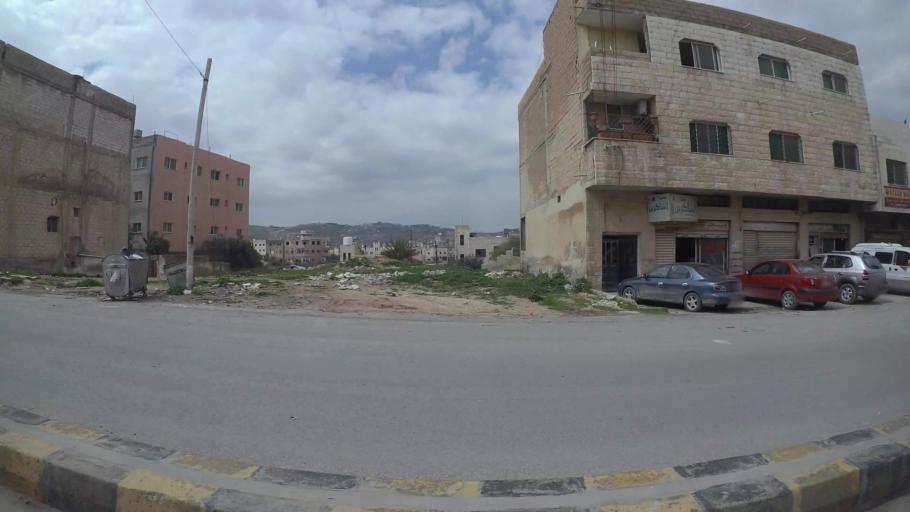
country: JO
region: Amman
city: Al Jubayhah
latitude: 32.0541
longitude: 35.8299
